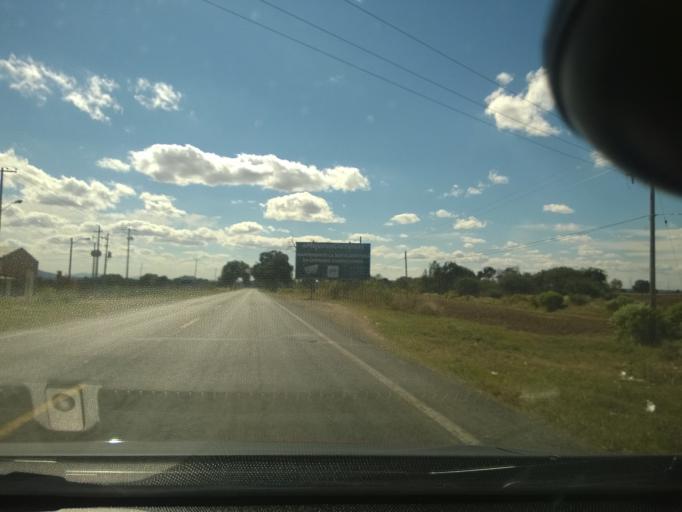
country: MX
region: Guanajuato
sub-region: Silao de la Victoria
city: La Aldea
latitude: 20.8891
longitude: -101.4935
